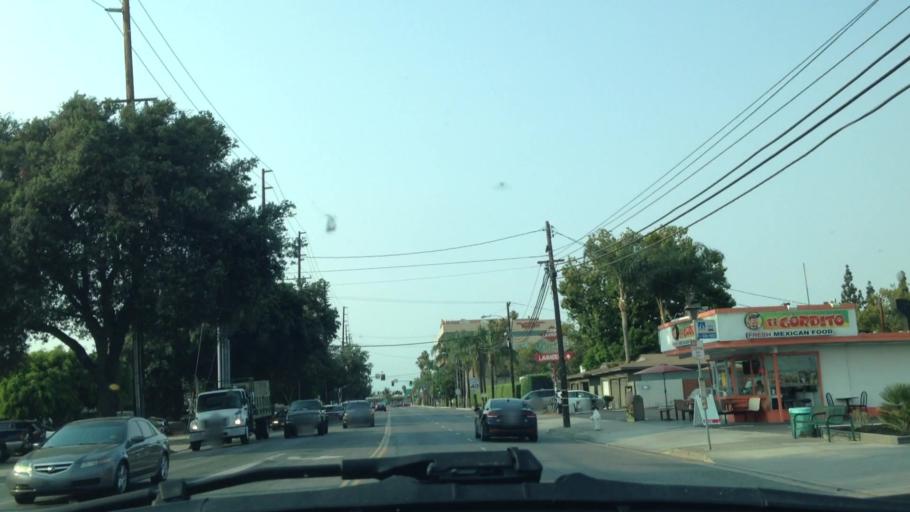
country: US
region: California
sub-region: Orange County
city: Santa Ana
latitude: 33.7483
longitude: -117.8518
